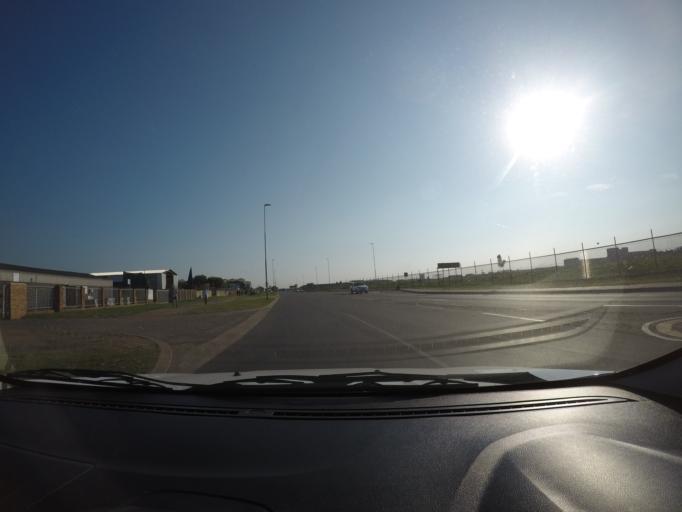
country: ZA
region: KwaZulu-Natal
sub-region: uThungulu District Municipality
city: Richards Bay
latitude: -28.7439
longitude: 32.0344
